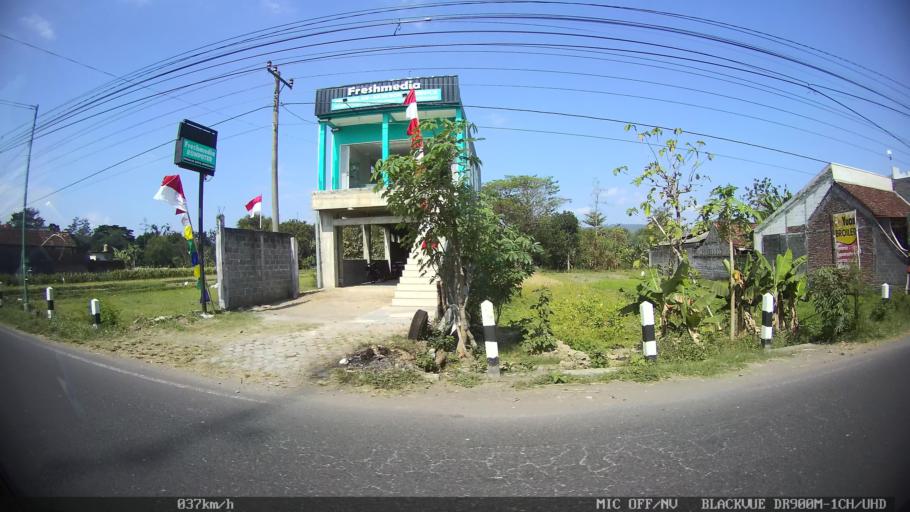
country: ID
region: Daerah Istimewa Yogyakarta
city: Sewon
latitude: -7.8973
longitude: 110.3847
